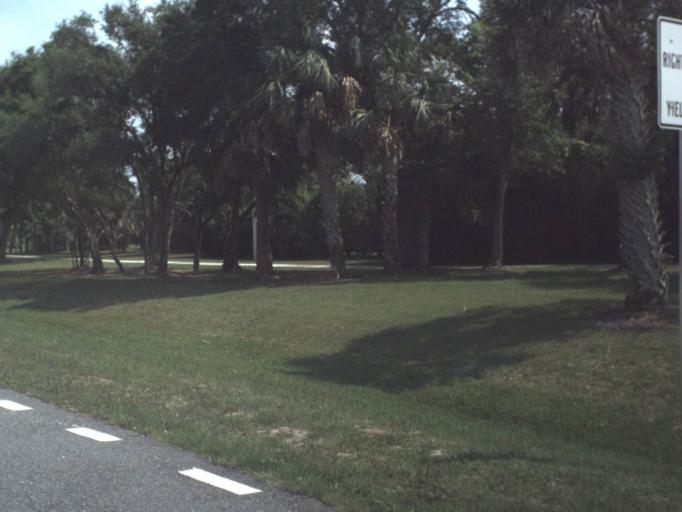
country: US
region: Florida
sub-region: Saint Johns County
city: Palm Valley
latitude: 30.1665
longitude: -81.3665
